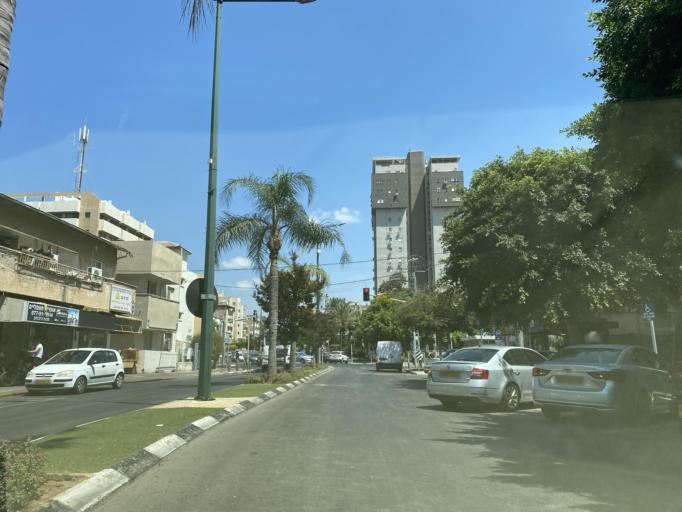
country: IL
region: Tel Aviv
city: Ramat HaSharon
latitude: 32.1671
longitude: 34.8480
